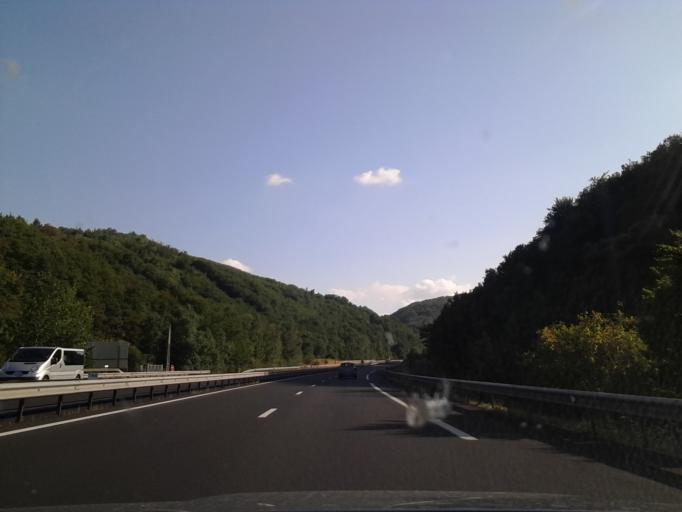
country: FR
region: Auvergne
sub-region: Departement du Cantal
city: Massiac
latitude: 45.2238
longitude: 3.2064
